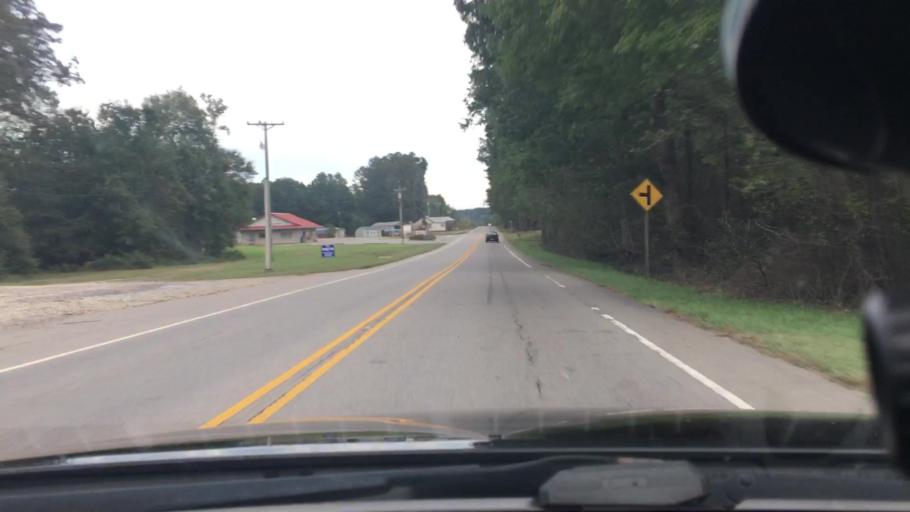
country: US
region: North Carolina
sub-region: Moore County
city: Carthage
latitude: 35.3861
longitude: -79.4965
